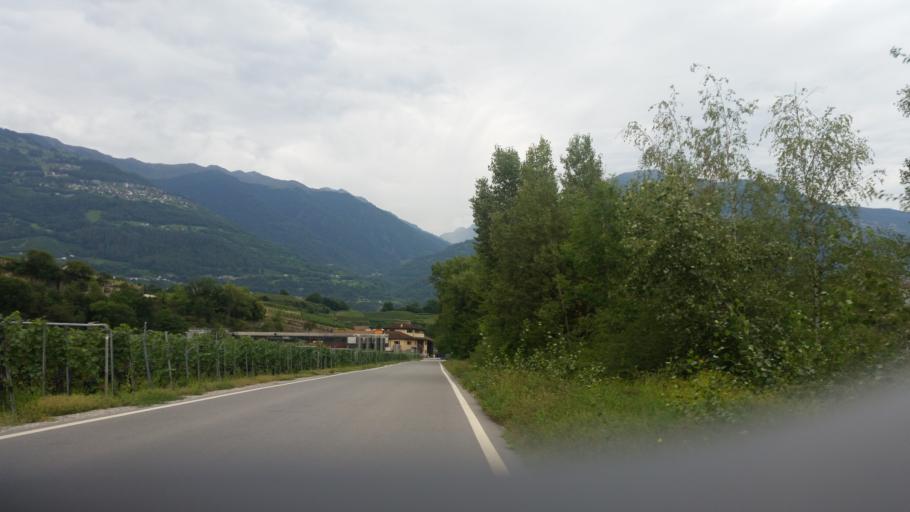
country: CH
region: Valais
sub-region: Conthey District
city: Conthey
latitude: 46.2281
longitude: 7.3132
